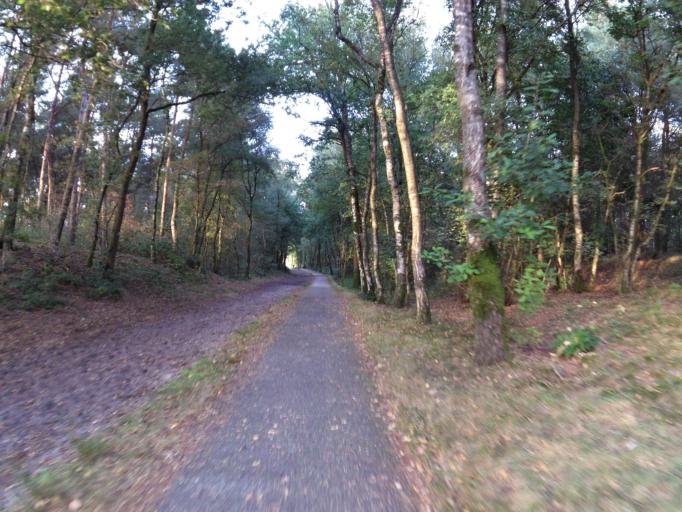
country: NL
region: Gelderland
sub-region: Gemeente Nijmegen
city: Lindenholt
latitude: 51.7802
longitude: 5.8078
